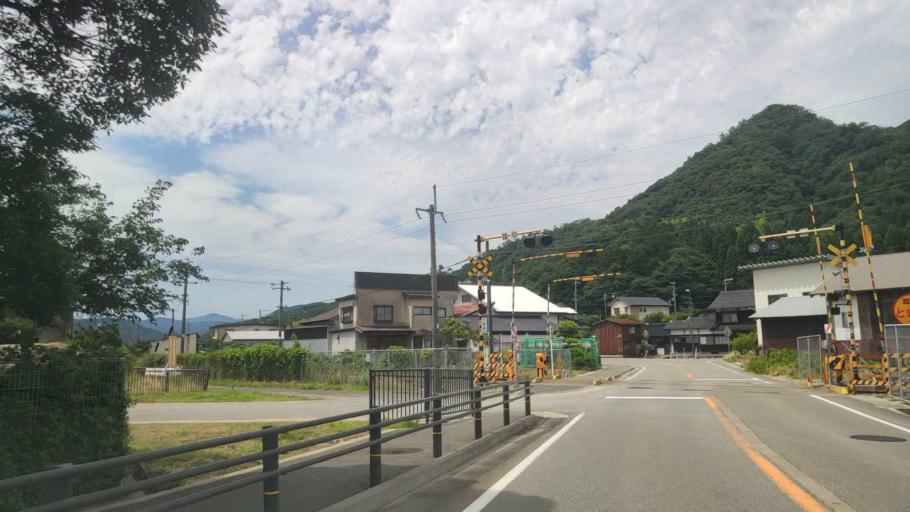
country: JP
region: Hyogo
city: Toyooka
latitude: 35.6468
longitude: 134.7586
